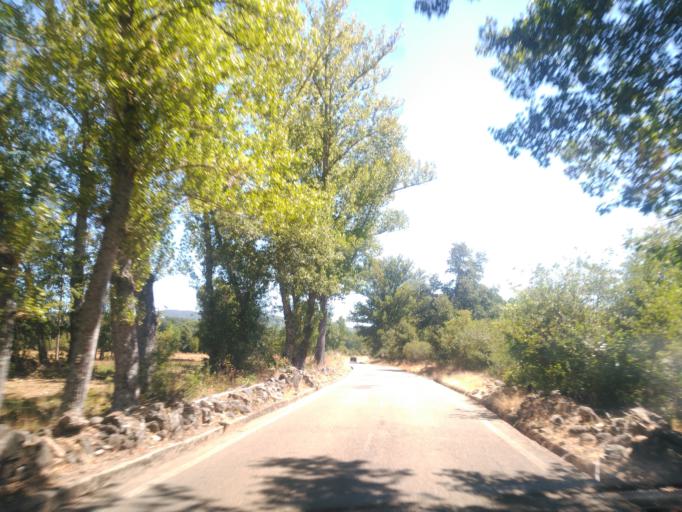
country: ES
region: Castille and Leon
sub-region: Provincia de Zamora
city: Galende
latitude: 42.0876
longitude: -6.6757
